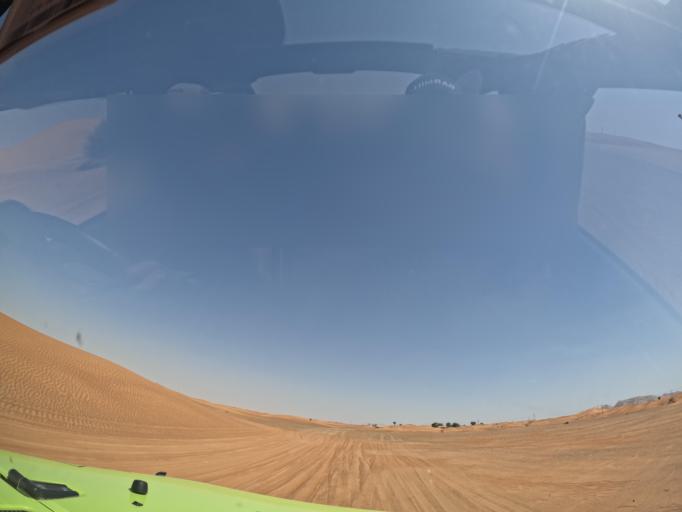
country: AE
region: Ash Shariqah
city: Adh Dhayd
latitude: 25.0113
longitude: 55.7412
